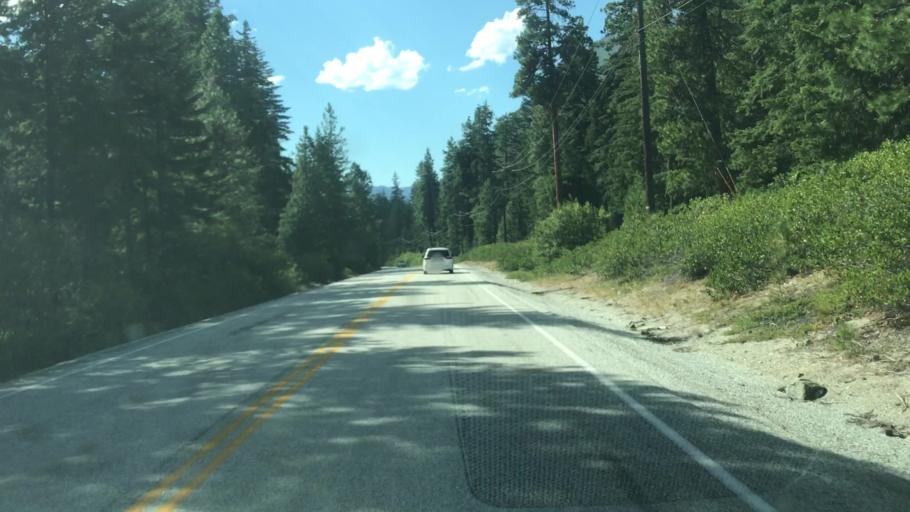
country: US
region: Washington
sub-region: Chelan County
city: Leavenworth
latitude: 47.8232
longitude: -120.7516
